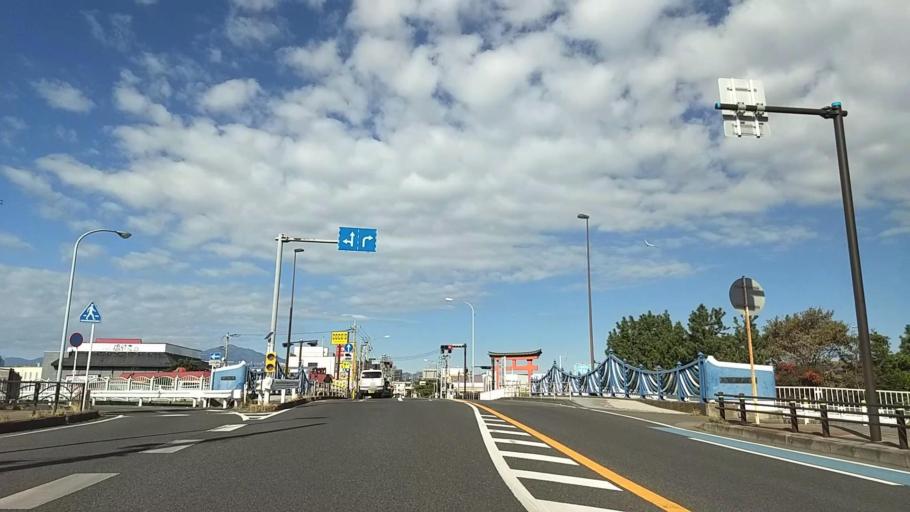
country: JP
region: Kanagawa
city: Chigasaki
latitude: 35.3294
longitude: 139.3902
